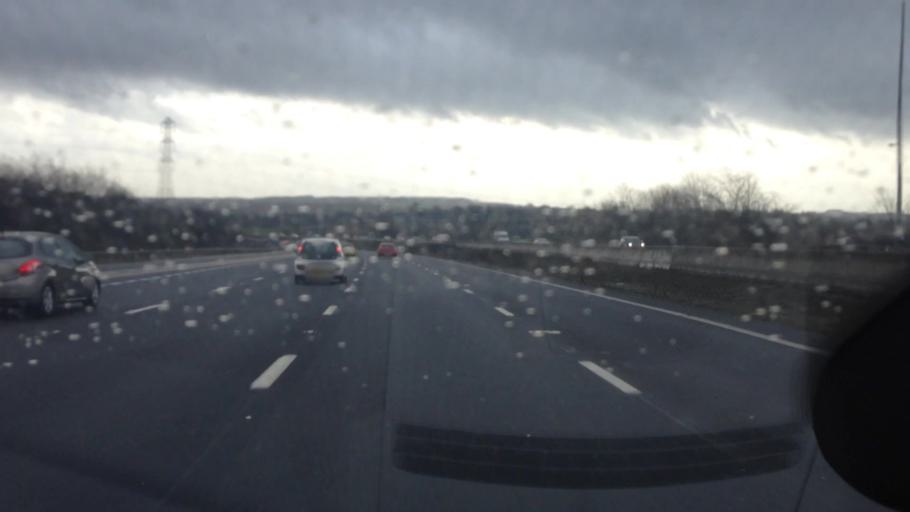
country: GB
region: England
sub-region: City and Borough of Wakefield
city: Horbury
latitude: 53.6786
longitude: -1.5537
